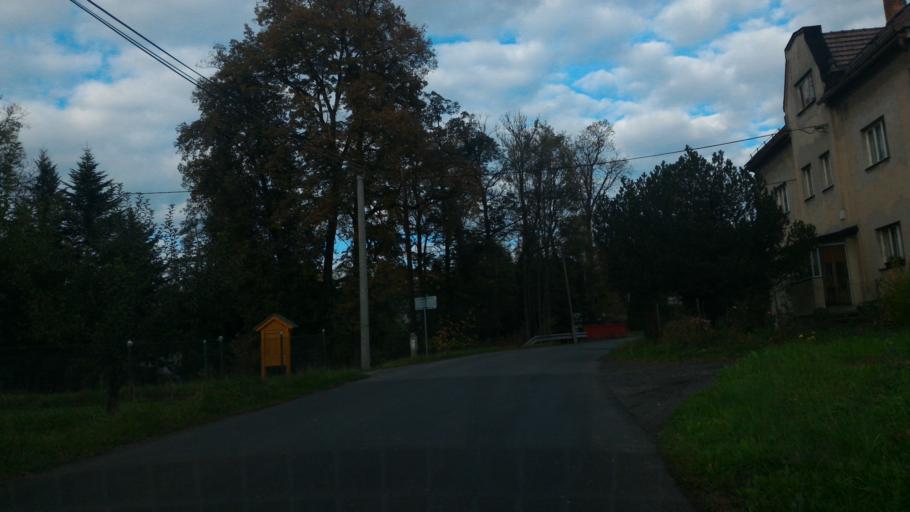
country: CZ
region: Ustecky
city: Benesov nad Ploucnici
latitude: 50.7698
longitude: 14.3479
